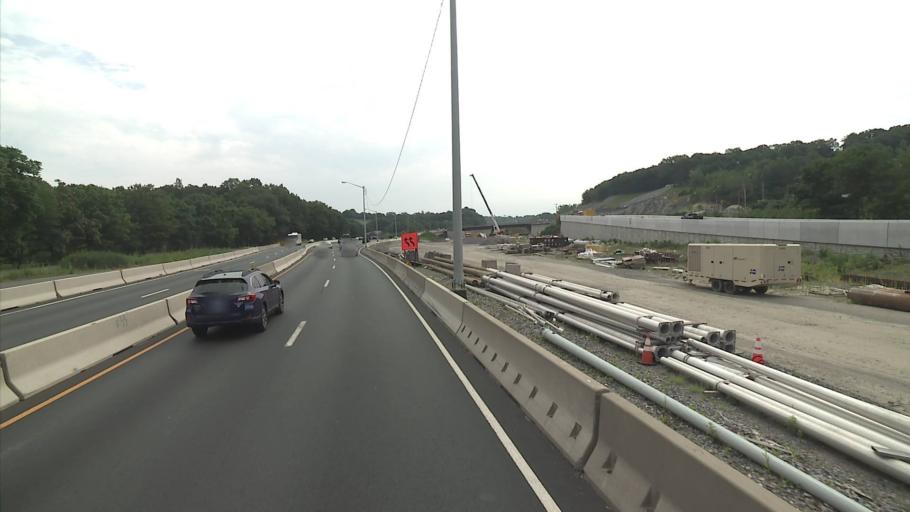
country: US
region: Connecticut
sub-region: New Haven County
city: Waterbury
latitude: 41.5396
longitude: -73.0149
